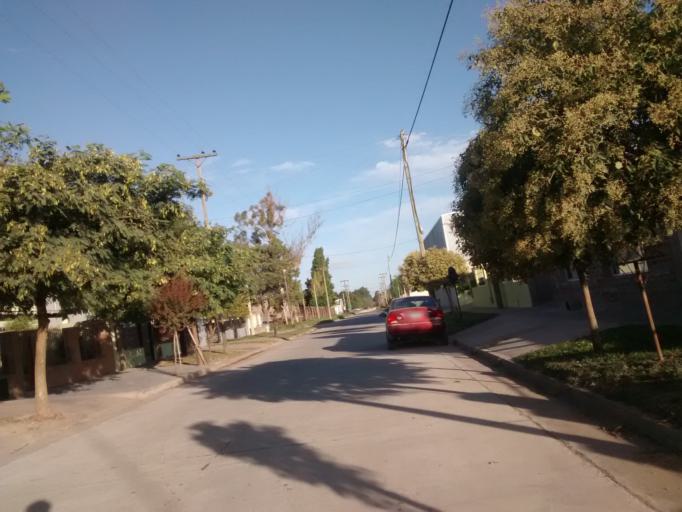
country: AR
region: Buenos Aires
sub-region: Partido de Loberia
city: Loberia
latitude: -38.1729
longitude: -58.7754
